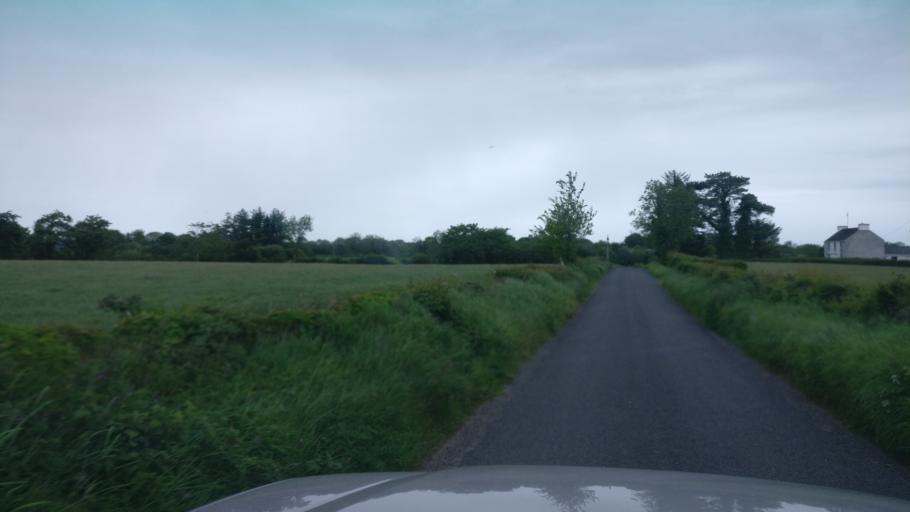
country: IE
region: Connaught
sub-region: County Galway
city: Loughrea
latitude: 53.1285
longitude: -8.4178
